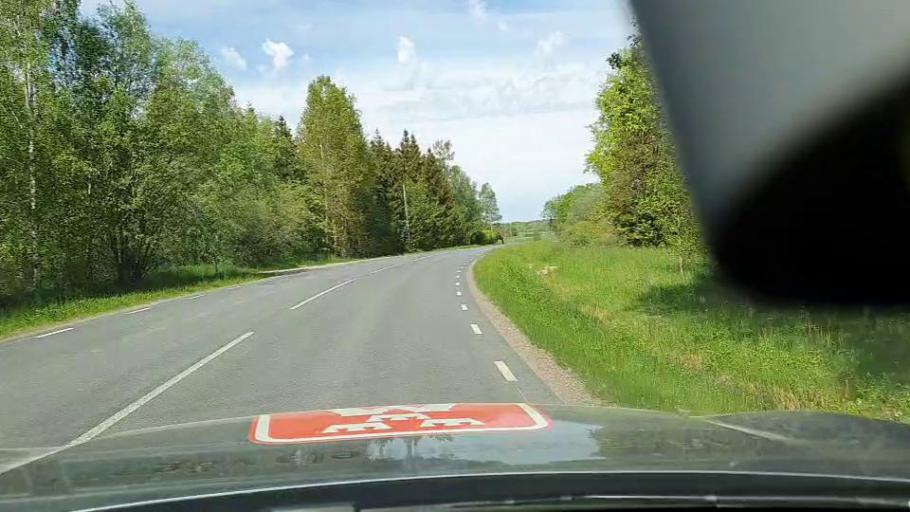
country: SE
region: Soedermanland
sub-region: Eskilstuna Kommun
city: Skogstorp
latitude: 59.3025
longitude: 16.4609
